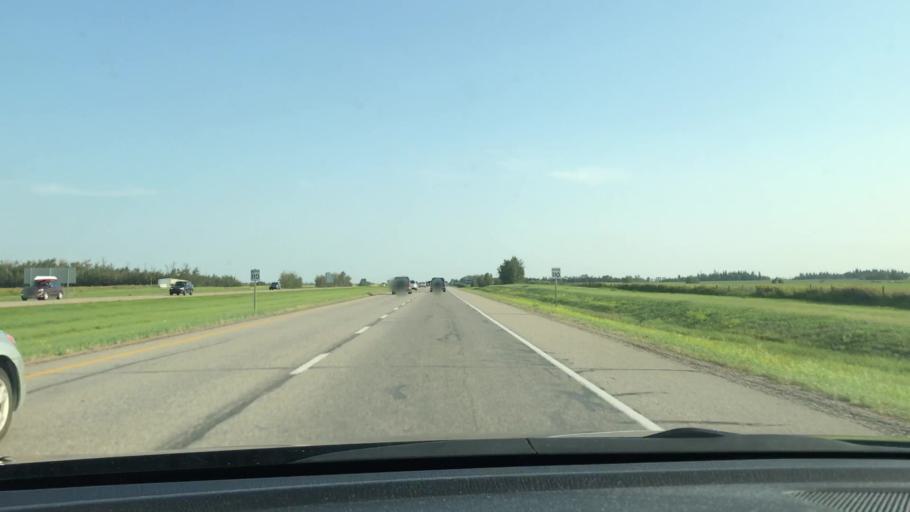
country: CA
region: Alberta
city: Millet
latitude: 53.0834
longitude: -113.5984
